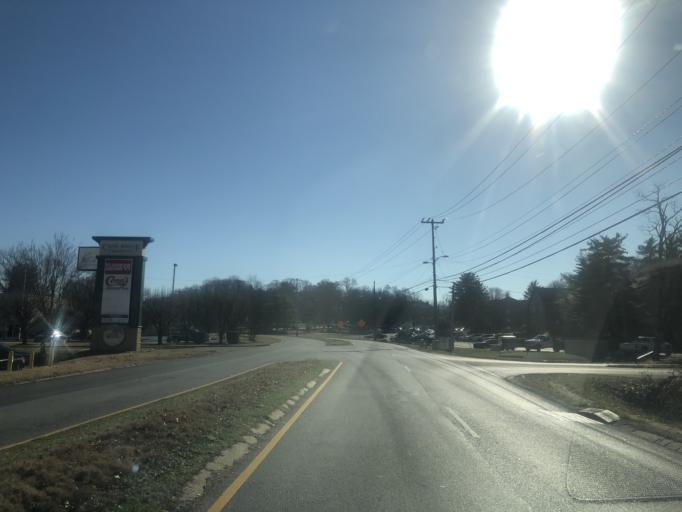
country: US
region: Tennessee
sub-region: Rutherford County
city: La Vergne
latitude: 36.0434
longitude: -86.6616
